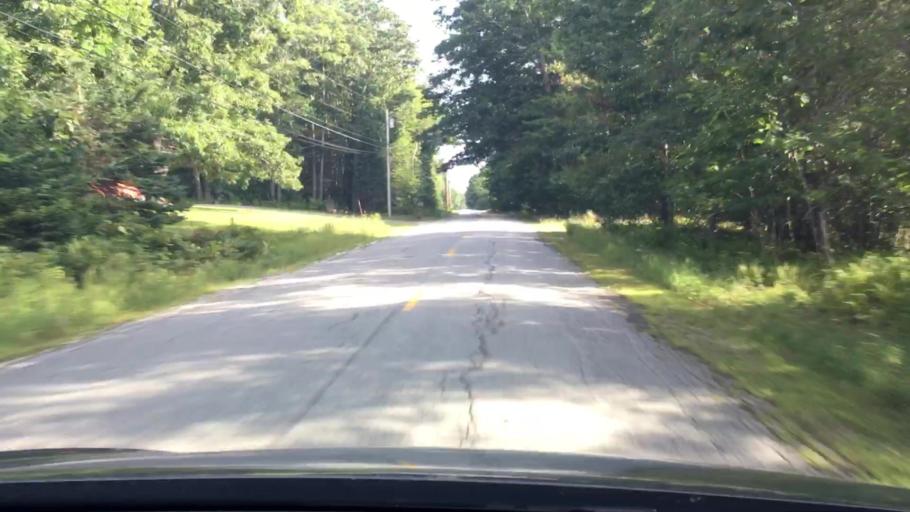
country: US
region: Maine
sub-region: Hancock County
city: Bucksport
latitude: 44.5402
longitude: -68.7953
